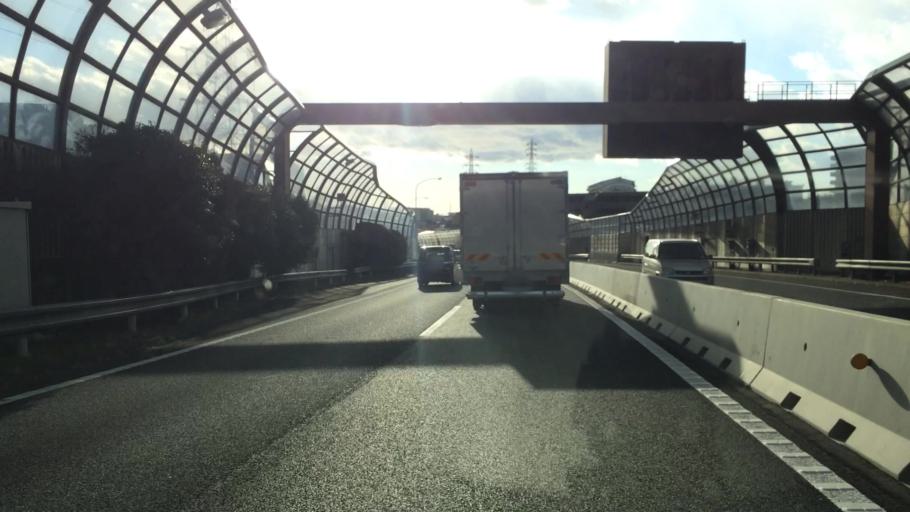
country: JP
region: Kanagawa
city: Yokohama
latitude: 35.4263
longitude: 139.5425
